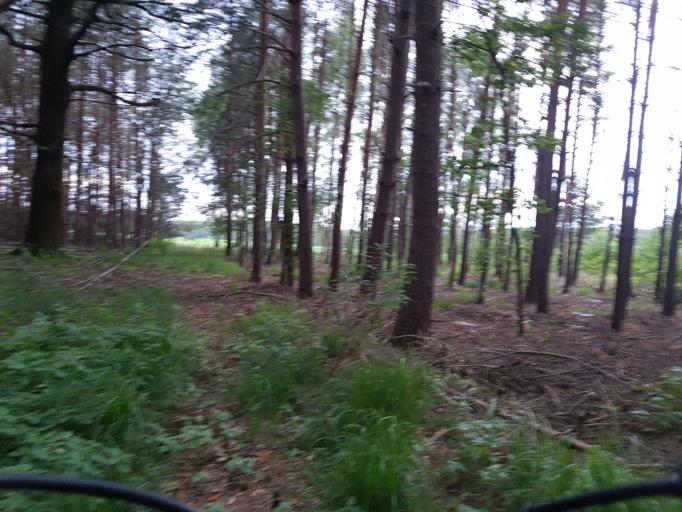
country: DE
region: Brandenburg
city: Schilda
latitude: 51.5826
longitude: 13.3540
